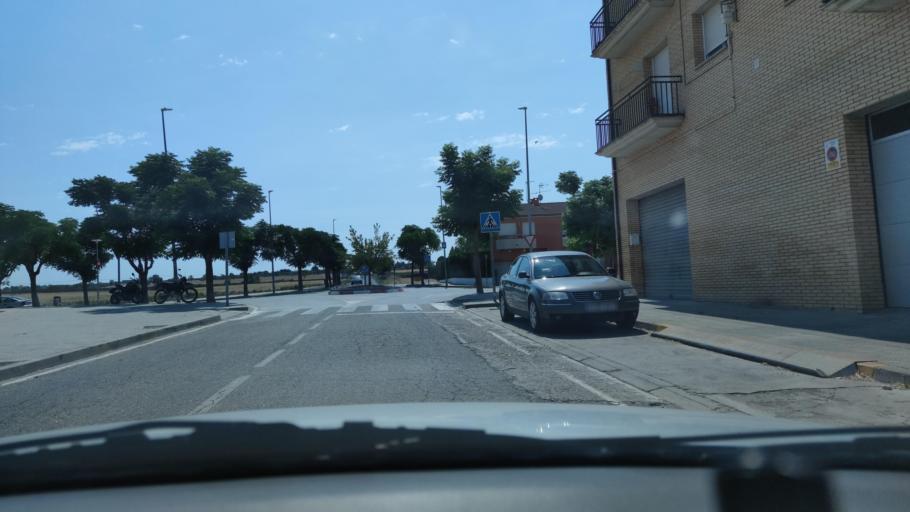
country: ES
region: Catalonia
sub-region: Provincia de Lleida
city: Ivorra
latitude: 41.7837
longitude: 1.2958
